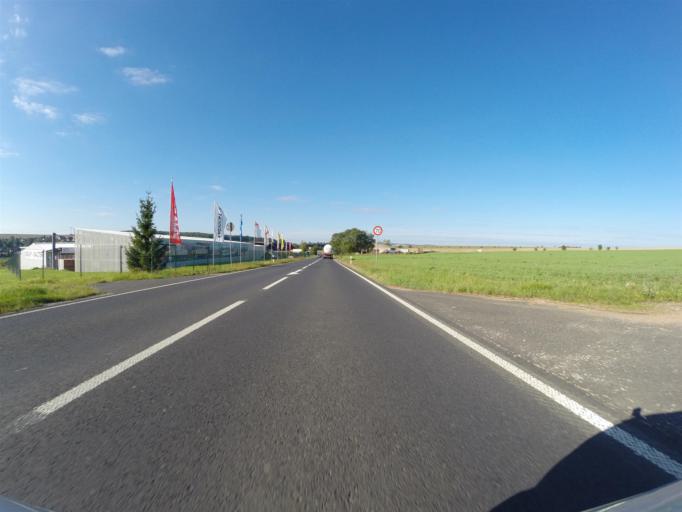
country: DE
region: Thuringia
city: Grossschwabhausen
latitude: 50.9433
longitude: 11.4907
